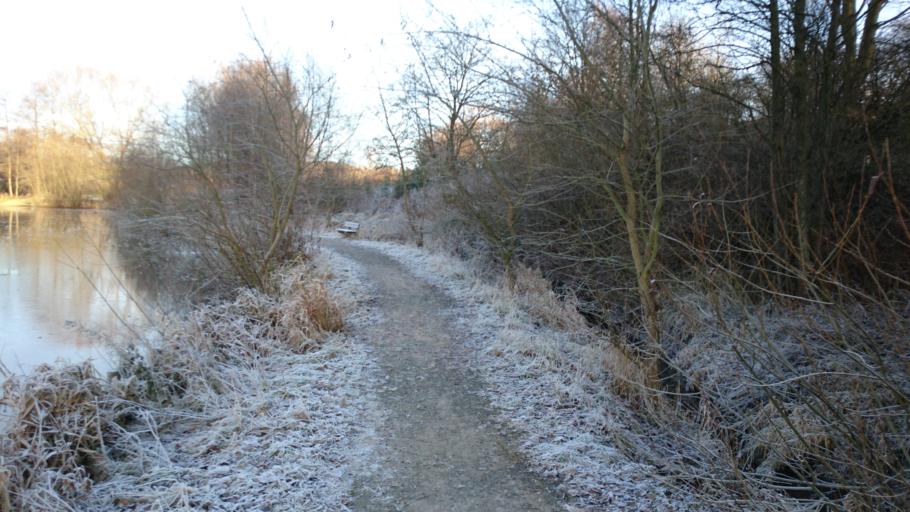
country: DE
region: Thuringia
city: Schleiz
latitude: 50.5832
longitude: 11.8275
